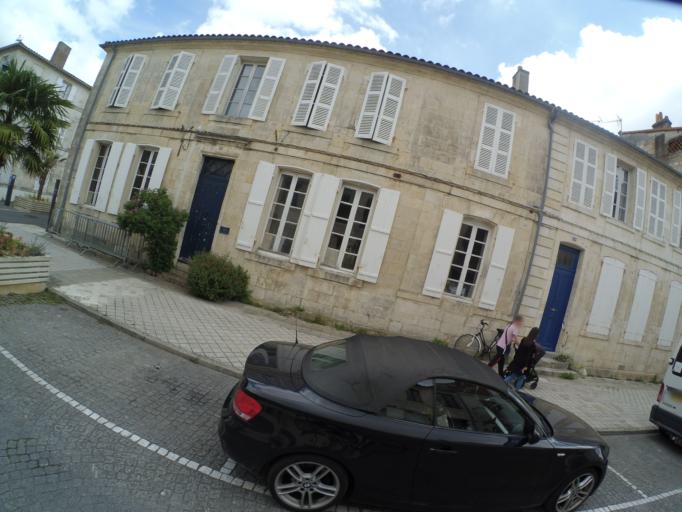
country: FR
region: Poitou-Charentes
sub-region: Departement de la Charente-Maritime
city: Rochefort
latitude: 45.9384
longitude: -0.9607
